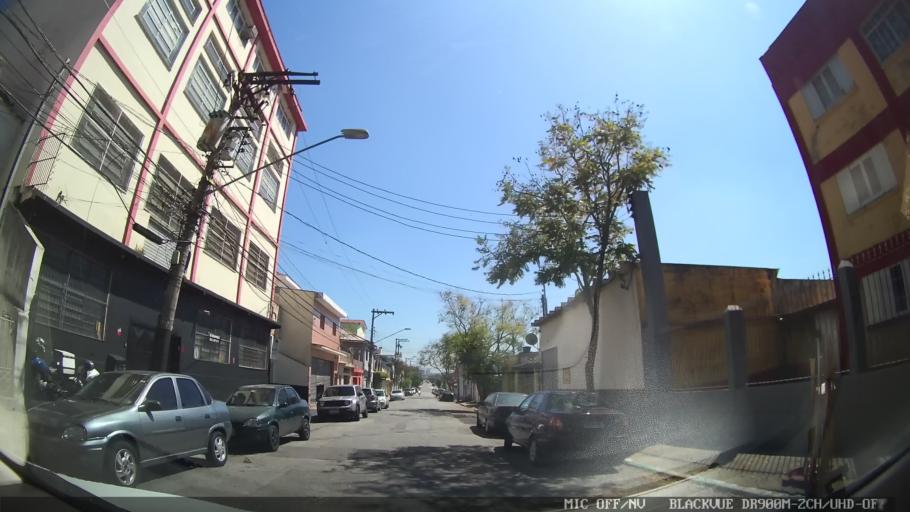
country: BR
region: Sao Paulo
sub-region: Sao Paulo
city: Sao Paulo
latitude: -23.5018
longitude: -46.6565
